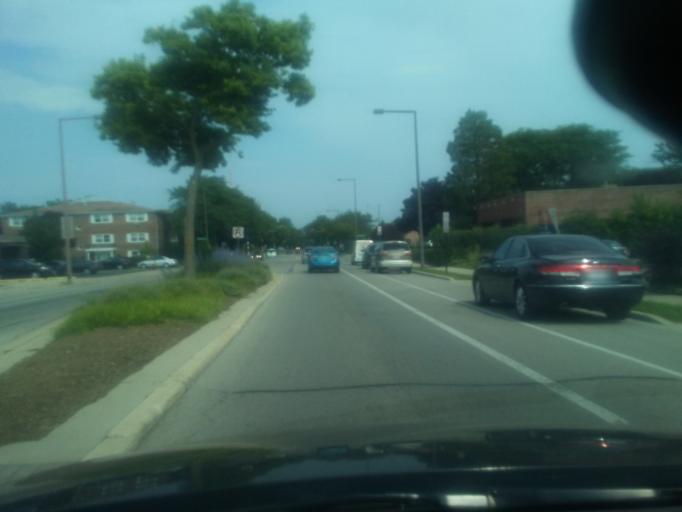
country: US
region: Illinois
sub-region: Cook County
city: Skokie
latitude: 42.0336
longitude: -87.7131
